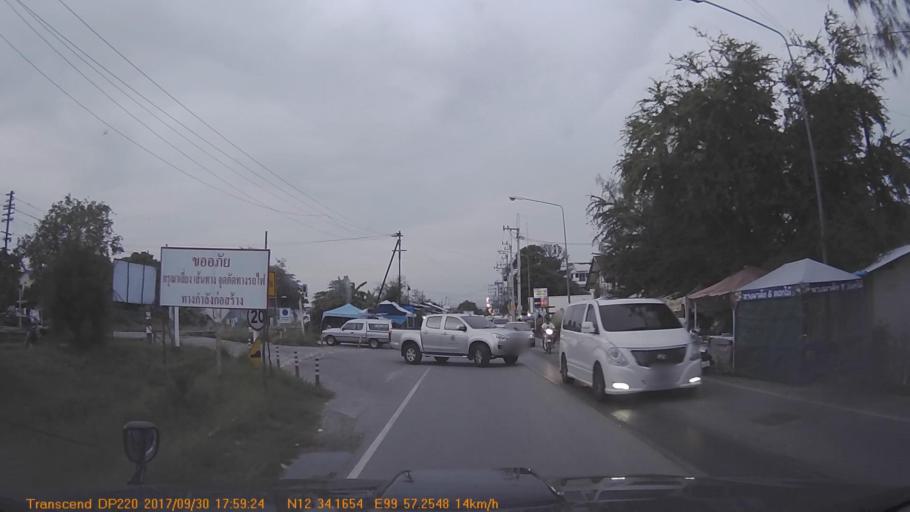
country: TH
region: Prachuap Khiri Khan
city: Hua Hin
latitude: 12.5695
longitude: 99.9542
